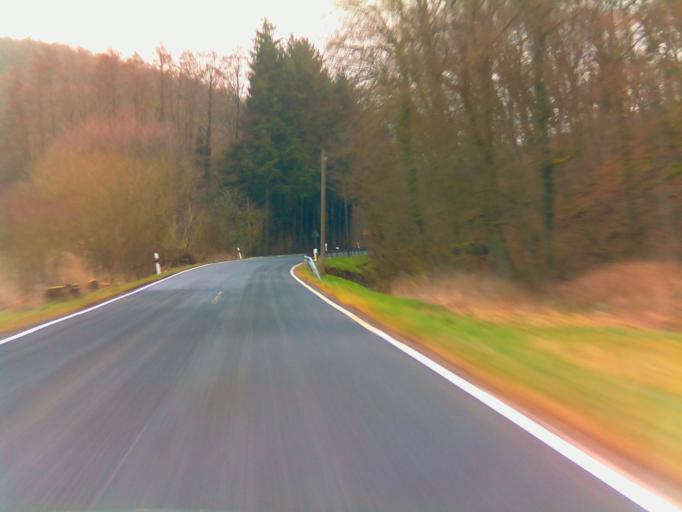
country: DE
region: Rheinland-Pfalz
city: Morsfeld
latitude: 49.7475
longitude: 7.9488
